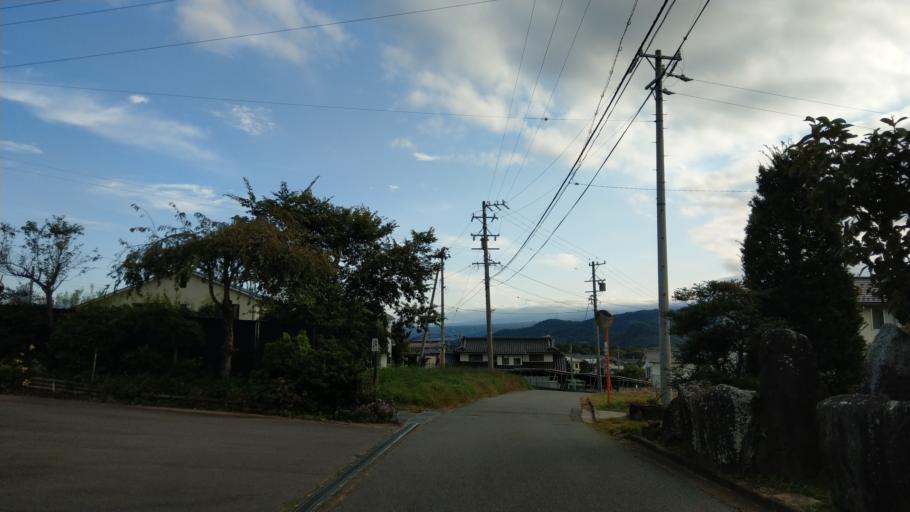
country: JP
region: Nagano
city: Komoro
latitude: 36.3377
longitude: 138.4203
